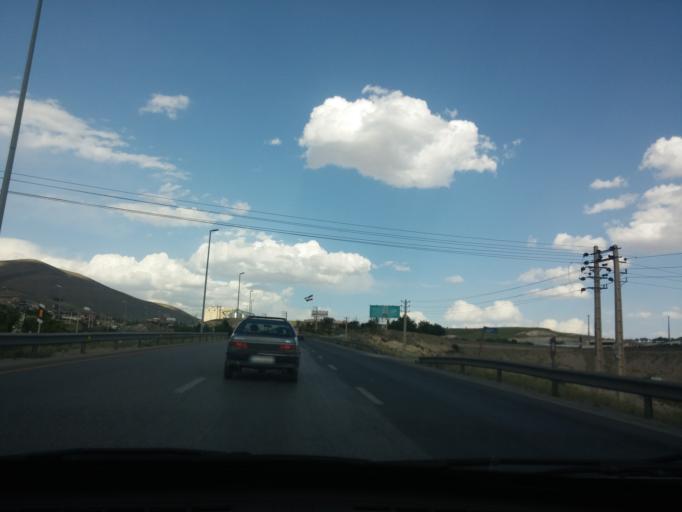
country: IR
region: Tehran
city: Damavand
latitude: 35.7176
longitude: 51.9303
